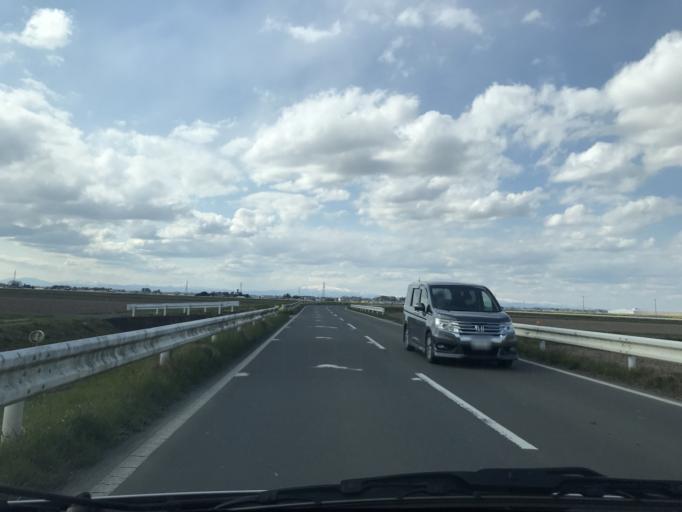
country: JP
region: Miyagi
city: Wakuya
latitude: 38.6523
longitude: 141.2395
